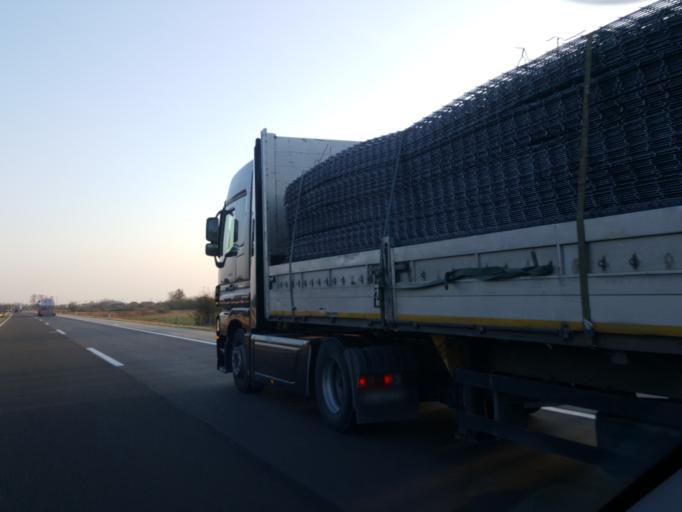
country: RS
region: Central Serbia
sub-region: Podunavski Okrug
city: Velika Plana
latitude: 44.3079
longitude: 21.0941
